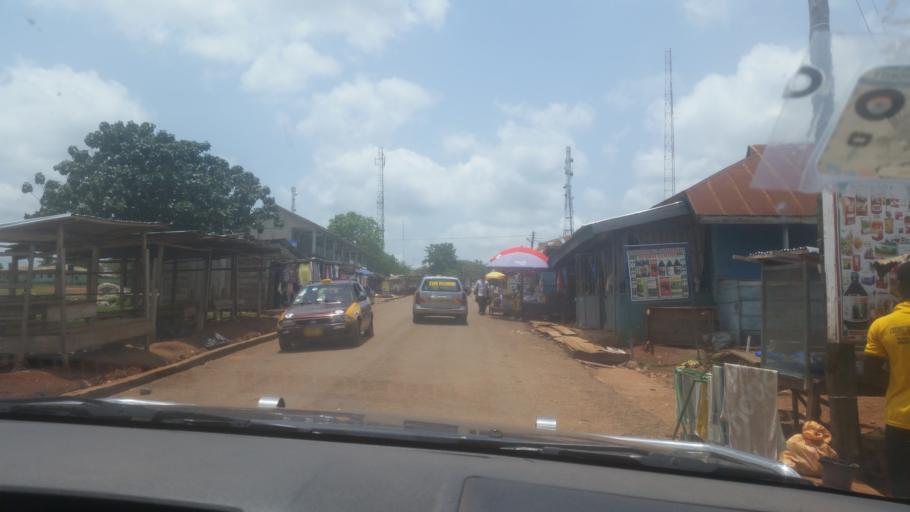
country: GH
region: Western
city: Bibiani
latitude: 6.8042
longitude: -2.5172
